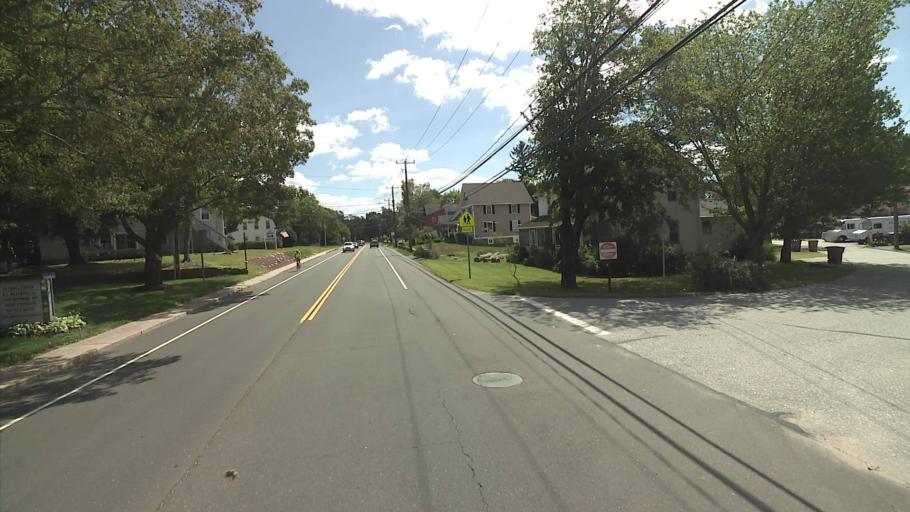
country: US
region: Connecticut
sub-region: New London County
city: Niantic
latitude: 41.3671
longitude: -72.2177
